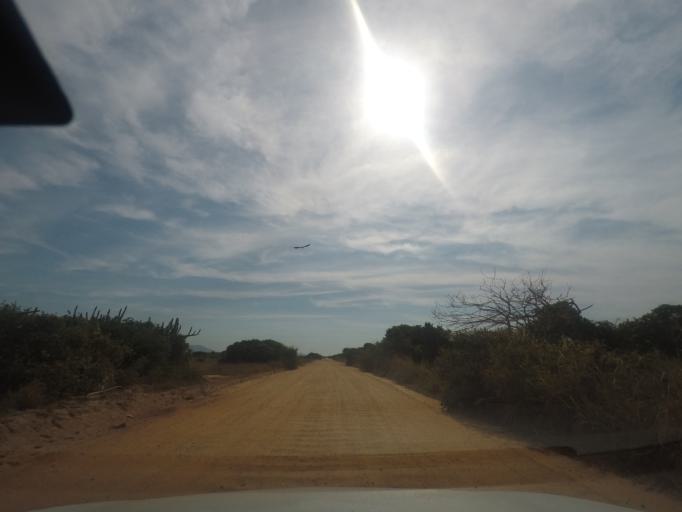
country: BR
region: Rio de Janeiro
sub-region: Marica
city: Marica
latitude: -22.9607
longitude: -42.8568
